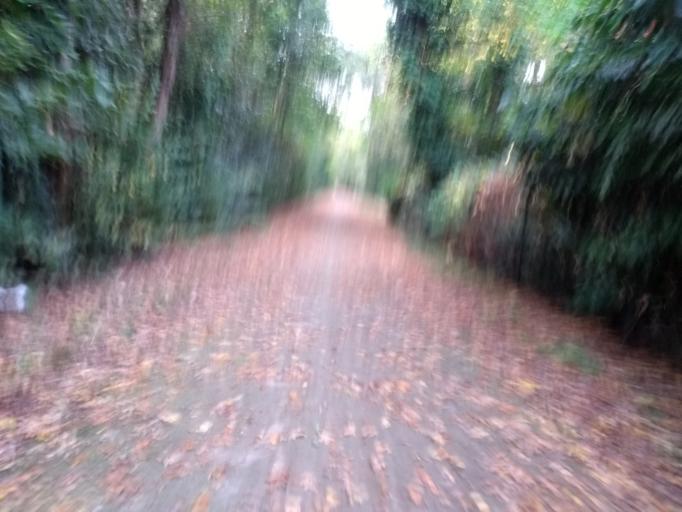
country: FR
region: Aquitaine
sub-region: Departement de la Gironde
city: Pessac
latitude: 44.7931
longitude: -0.6594
